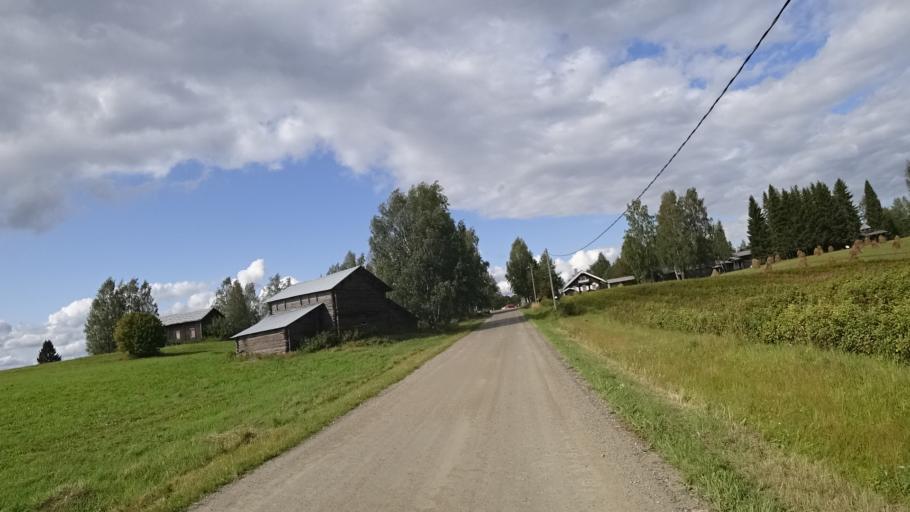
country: FI
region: North Karelia
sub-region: Joensuu
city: Ilomantsi
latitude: 62.6561
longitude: 30.9395
